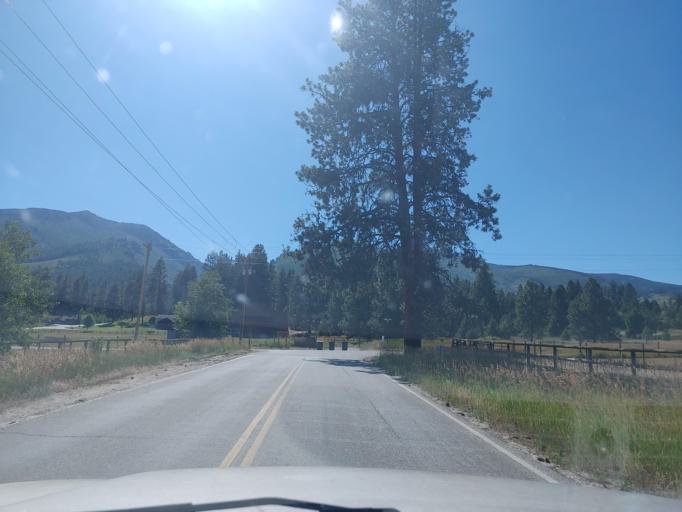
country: US
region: Montana
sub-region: Ravalli County
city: Hamilton
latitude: 46.3130
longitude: -114.2068
